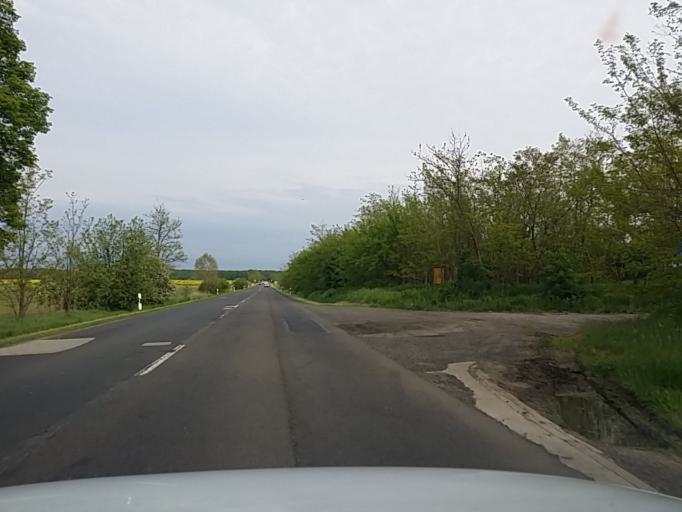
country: HU
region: Pest
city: Szentlorinckata
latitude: 47.5796
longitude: 19.7545
